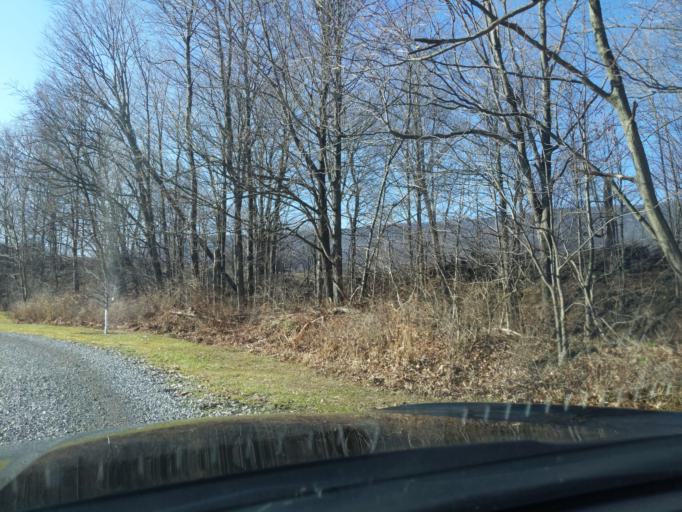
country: US
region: Pennsylvania
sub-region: Blair County
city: Bellwood
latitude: 40.5590
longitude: -78.2718
